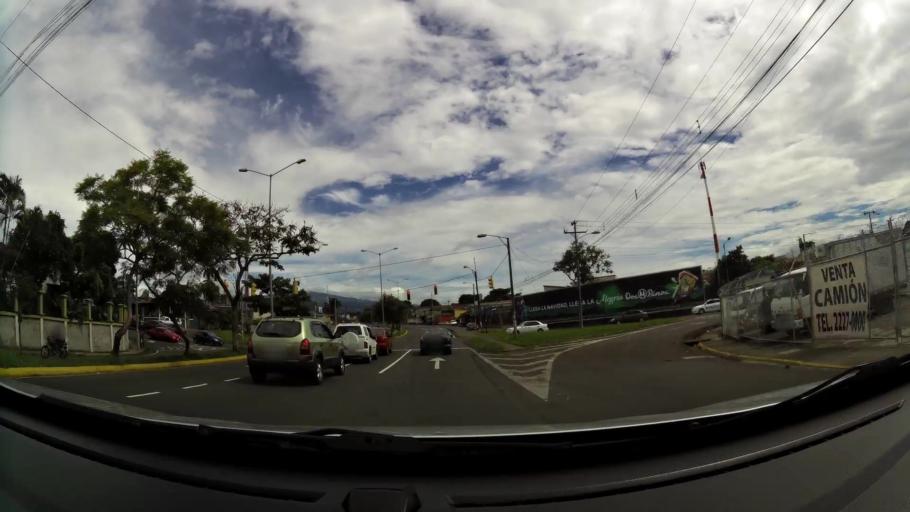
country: CR
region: San Jose
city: San Jose
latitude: 9.9220
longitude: -84.0689
